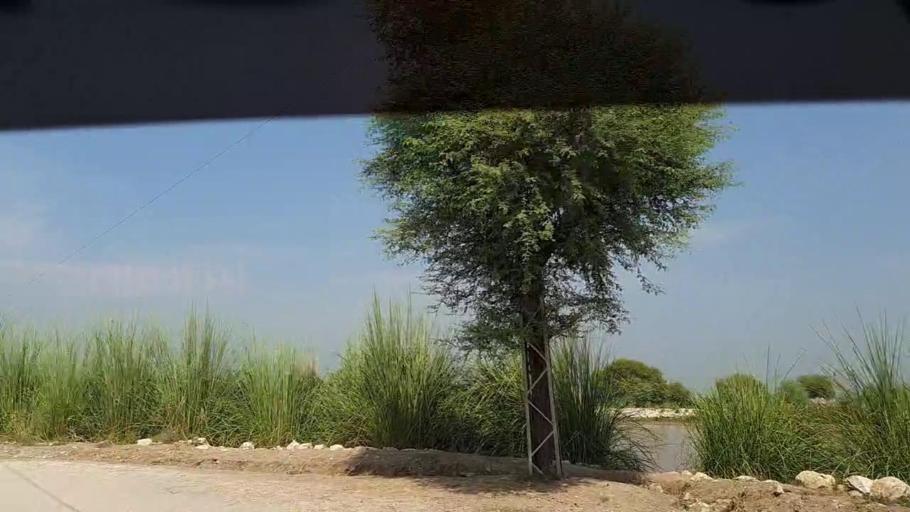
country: PK
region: Sindh
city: Thul
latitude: 28.1331
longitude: 68.7173
